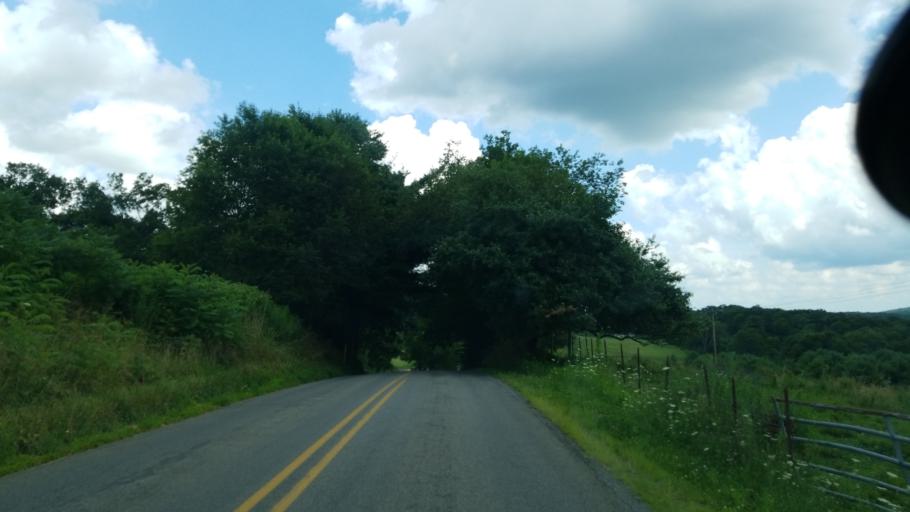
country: US
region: Pennsylvania
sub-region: Jefferson County
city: Brookville
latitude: 41.2324
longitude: -79.0707
